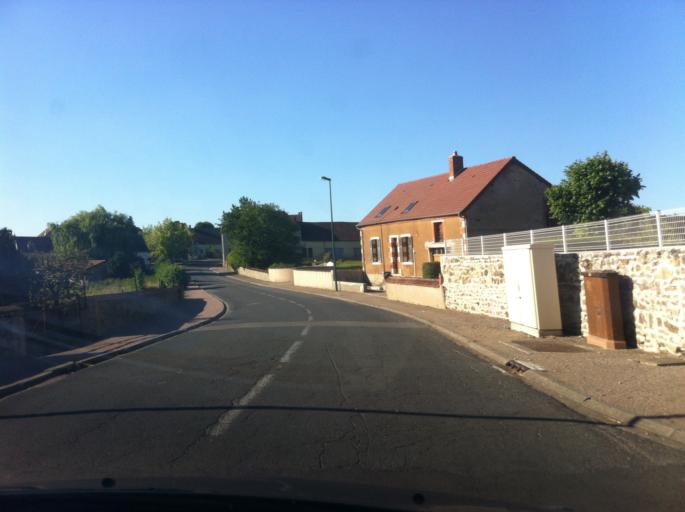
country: FR
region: Auvergne
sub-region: Departement de l'Allier
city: Chantelle
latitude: 46.2558
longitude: 3.1132
